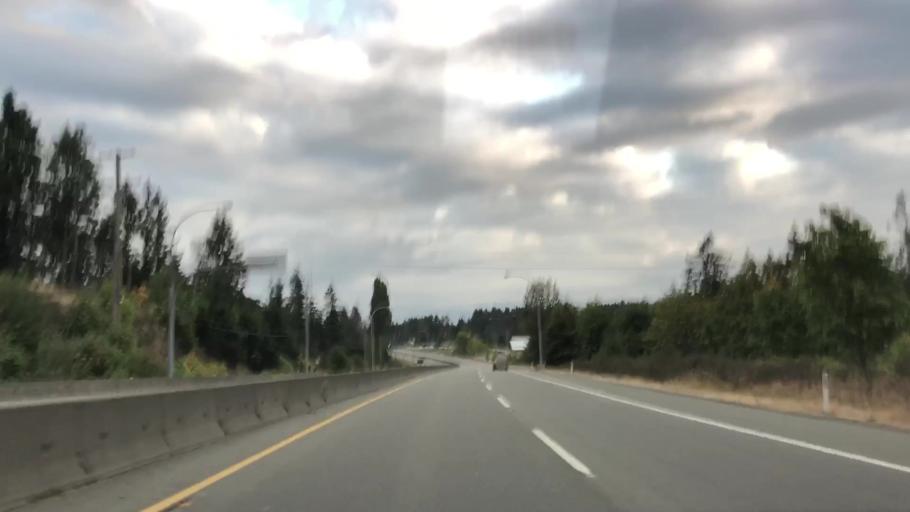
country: CA
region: British Columbia
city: North Saanich
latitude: 48.6586
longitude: -123.5606
